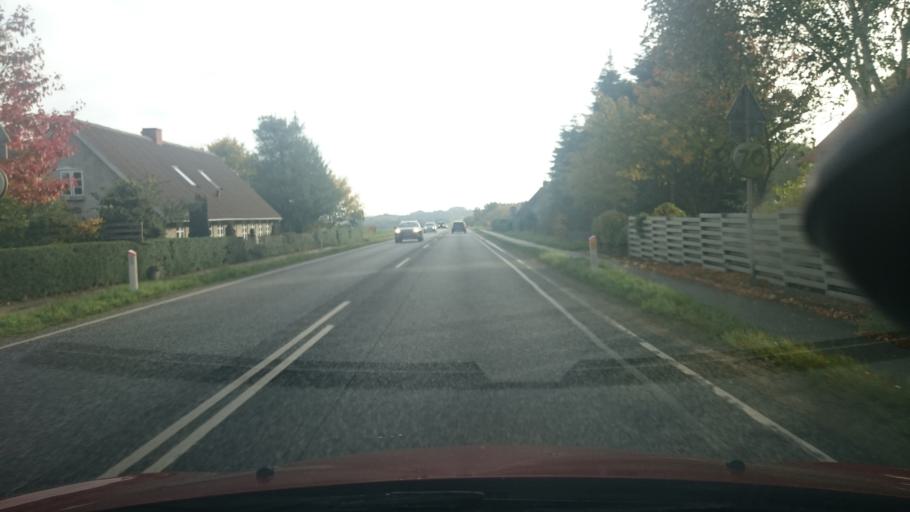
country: DK
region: Central Jutland
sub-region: Randers Kommune
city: Assentoft
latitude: 56.4418
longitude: 10.0969
